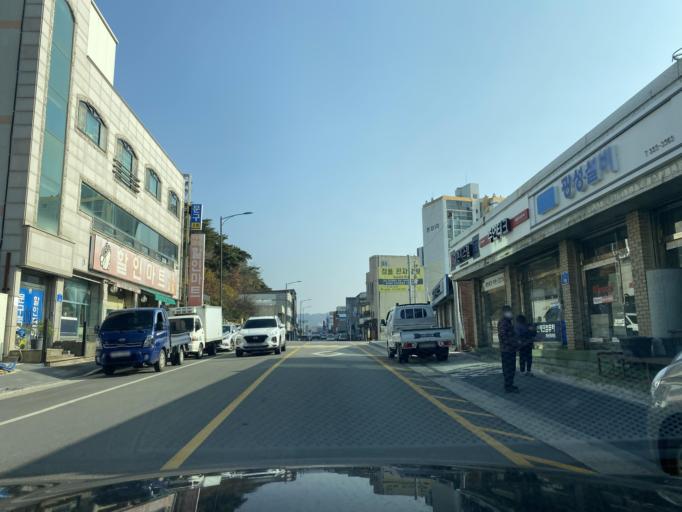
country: KR
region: Chungcheongnam-do
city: Yesan
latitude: 36.6799
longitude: 126.8360
